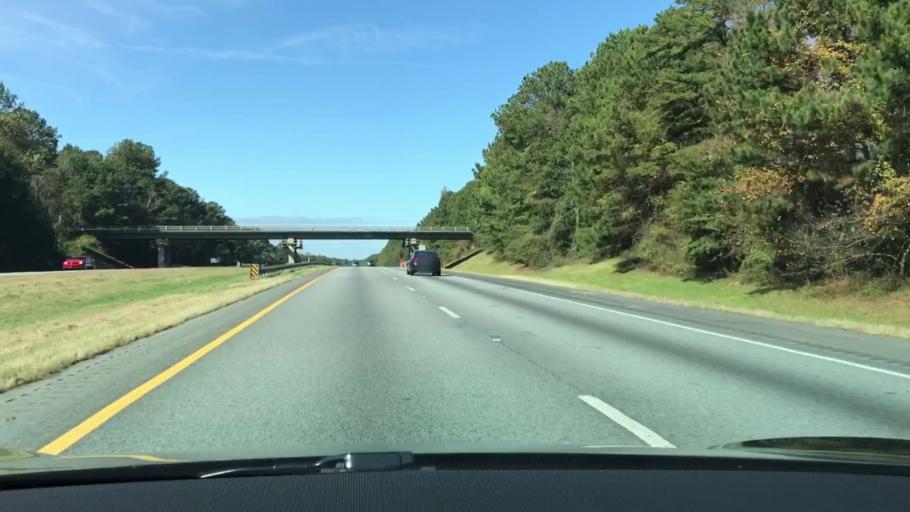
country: US
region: Georgia
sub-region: Morgan County
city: Madison
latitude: 33.5677
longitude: -83.5129
